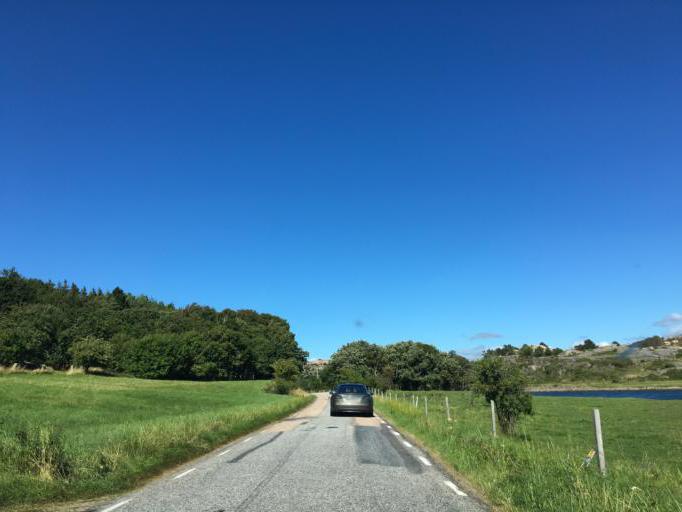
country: SE
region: Vaestra Goetaland
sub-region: Sotenas Kommun
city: Hunnebostrand
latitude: 58.4133
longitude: 11.2644
